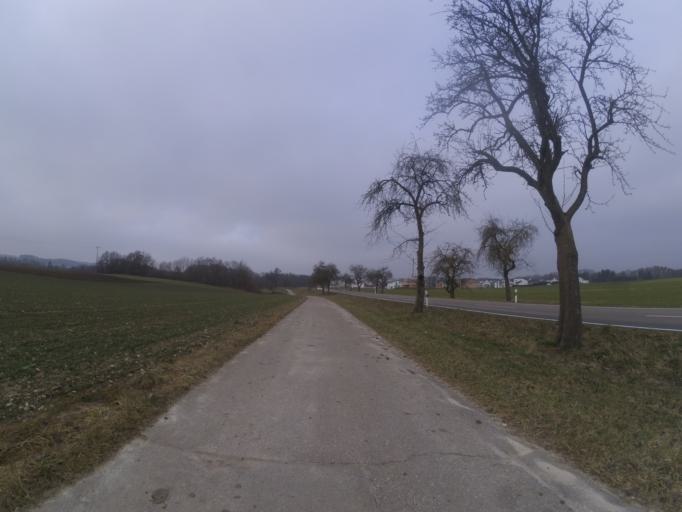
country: DE
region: Baden-Wuerttemberg
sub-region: Tuebingen Region
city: Untermarchtal
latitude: 48.2397
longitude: 9.6236
